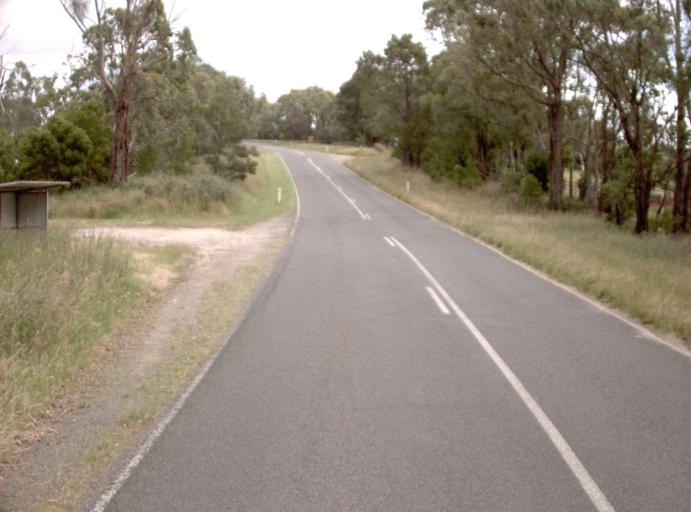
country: AU
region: Victoria
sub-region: Latrobe
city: Moe
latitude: -38.1019
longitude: 146.2379
